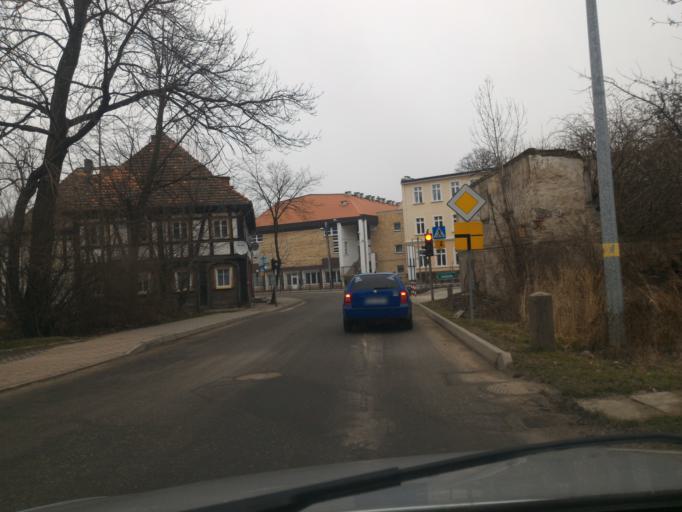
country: PL
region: Lower Silesian Voivodeship
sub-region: Powiat zgorzelecki
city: Bogatynia
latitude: 50.9041
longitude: 14.9543
